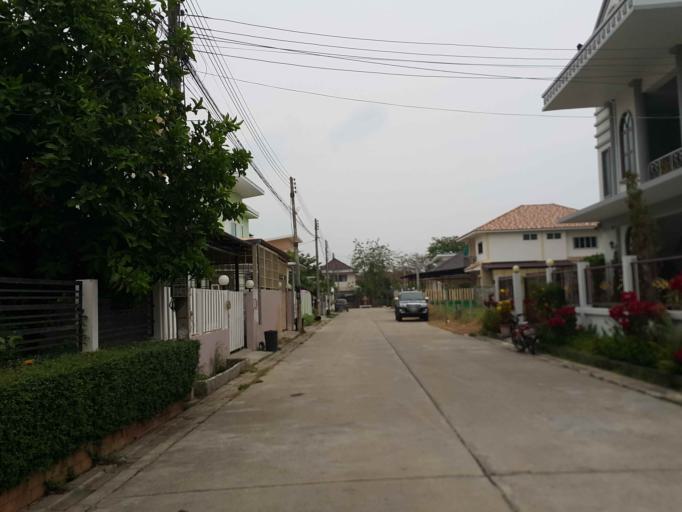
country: TH
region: Chiang Mai
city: Saraphi
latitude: 18.7513
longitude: 99.0127
